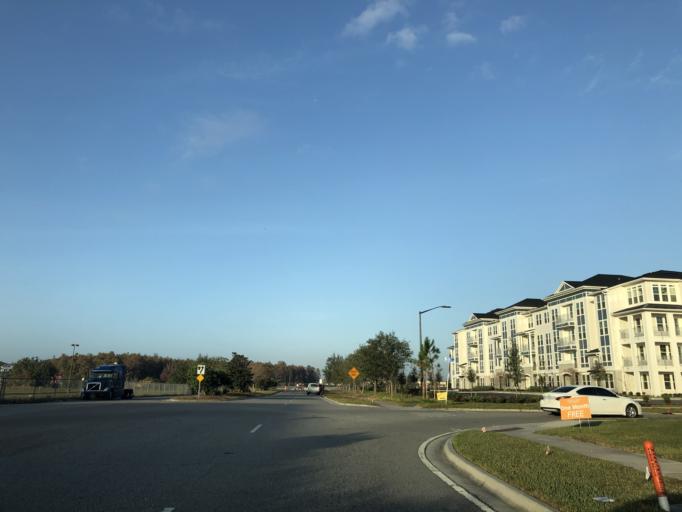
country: US
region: Florida
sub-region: Orange County
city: Hunters Creek
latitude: 28.3373
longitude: -81.4225
